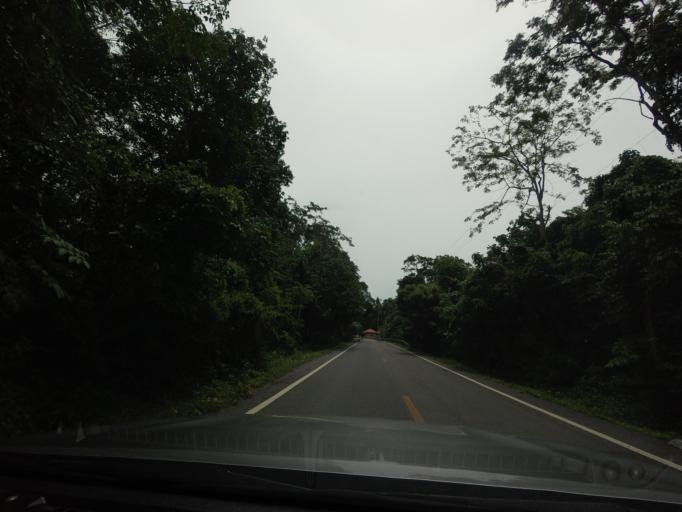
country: TH
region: Pattani
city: Kapho
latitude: 6.6261
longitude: 101.5463
